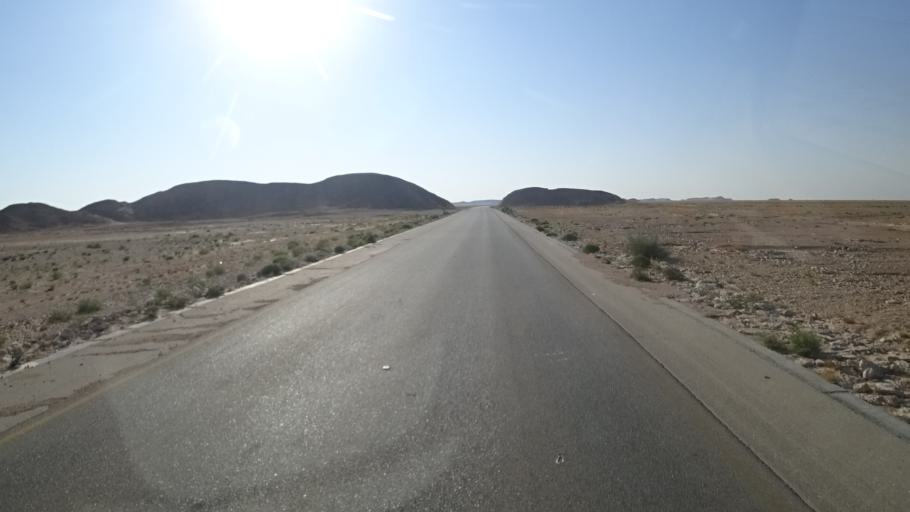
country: OM
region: Zufar
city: Salalah
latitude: 17.6394
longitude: 53.8923
